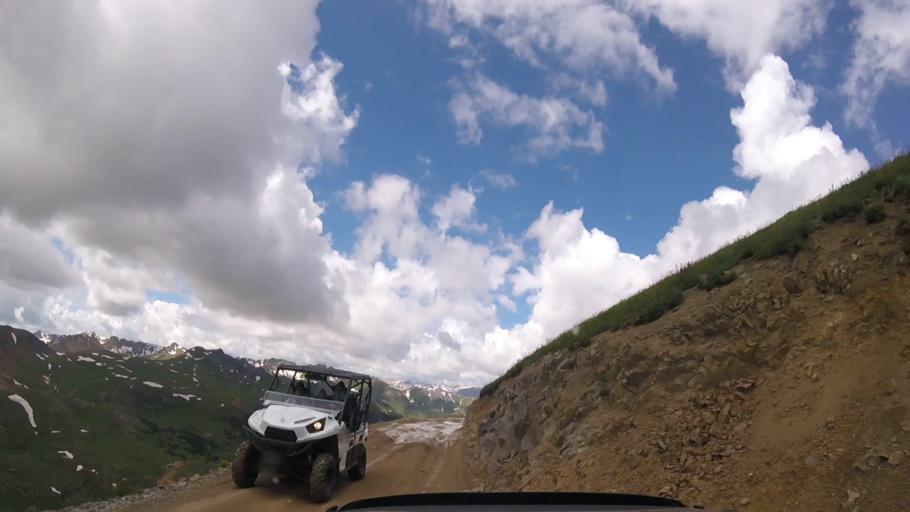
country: US
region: Colorado
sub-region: Ouray County
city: Ouray
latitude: 37.9657
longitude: -107.5825
